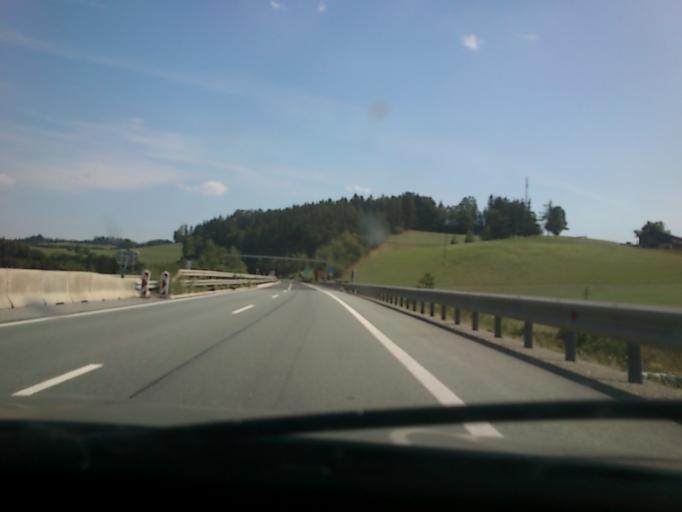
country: AT
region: Lower Austria
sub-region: Politischer Bezirk Neunkirchen
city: Zobern
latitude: 47.5238
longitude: 16.1085
